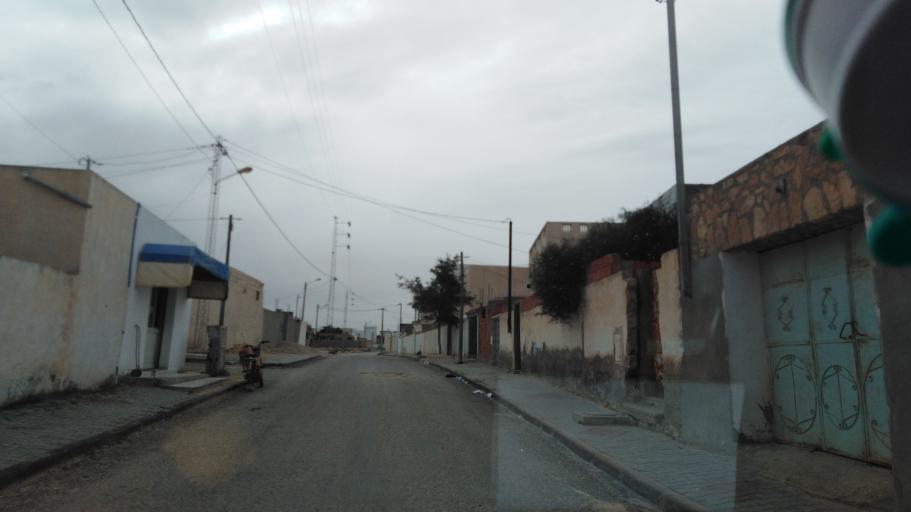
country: TN
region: Qabis
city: Gabes
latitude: 33.9551
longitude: 10.0042
